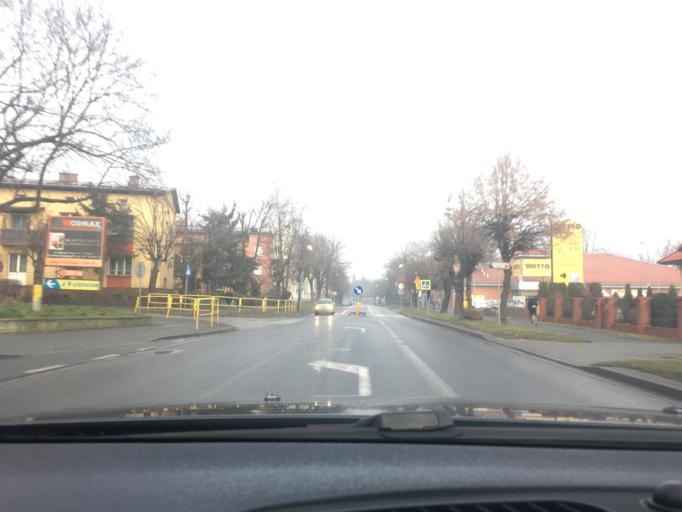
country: PL
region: Swietokrzyskie
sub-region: Powiat jedrzejowski
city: Jedrzejow
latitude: 50.6475
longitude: 20.2922
